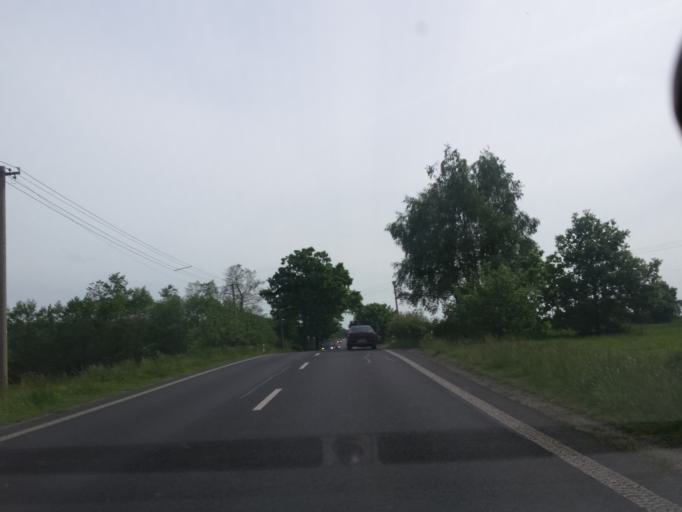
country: CZ
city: Novy Bor
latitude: 50.7218
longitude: 14.5457
